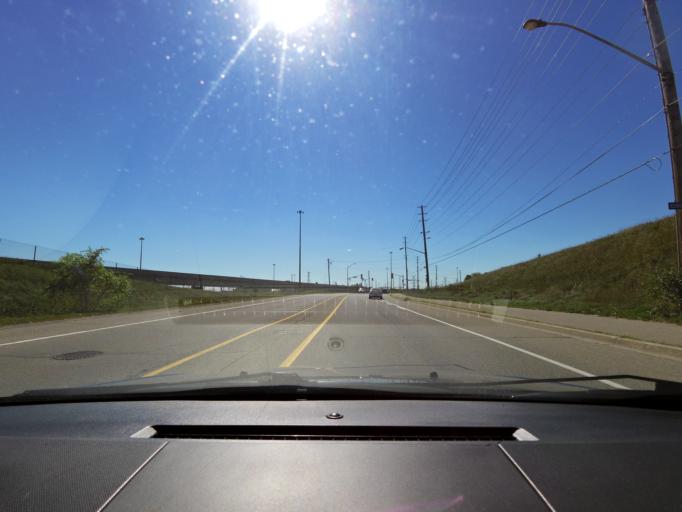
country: CA
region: Ontario
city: Burlington
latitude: 43.3391
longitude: -79.8327
